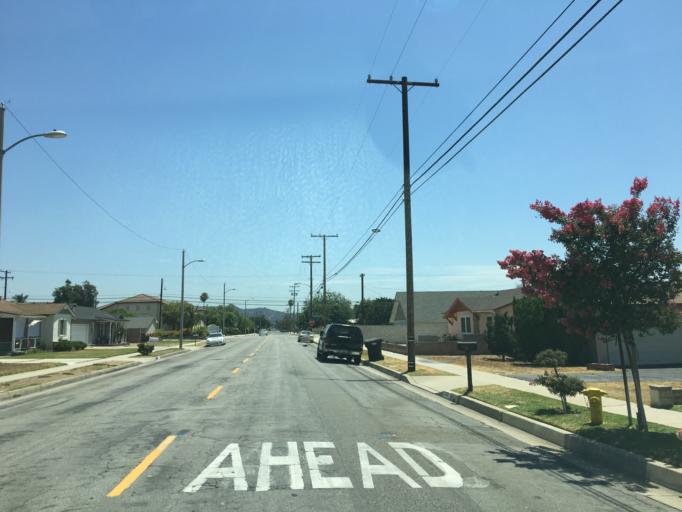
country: US
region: California
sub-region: Los Angeles County
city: Charter Oak
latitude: 34.1041
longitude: -117.8551
